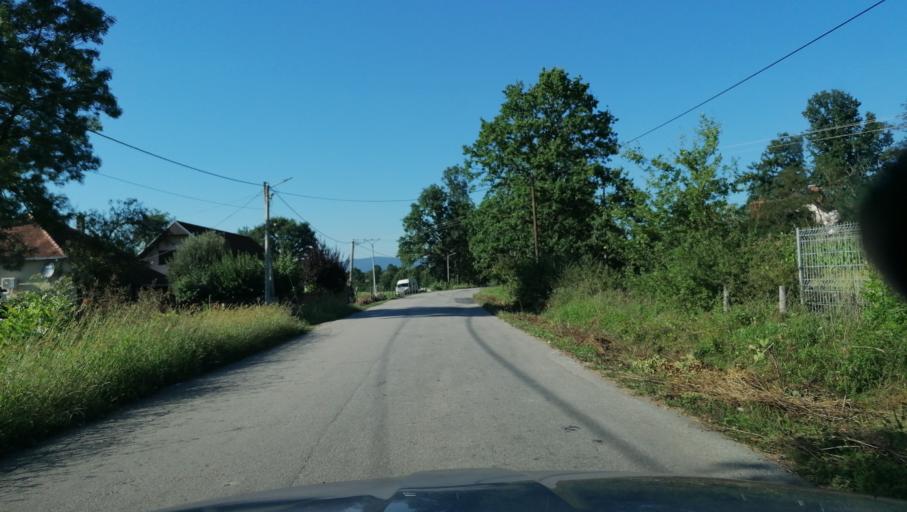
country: RS
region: Central Serbia
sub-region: Raski Okrug
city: Kraljevo
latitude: 43.8342
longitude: 20.5948
